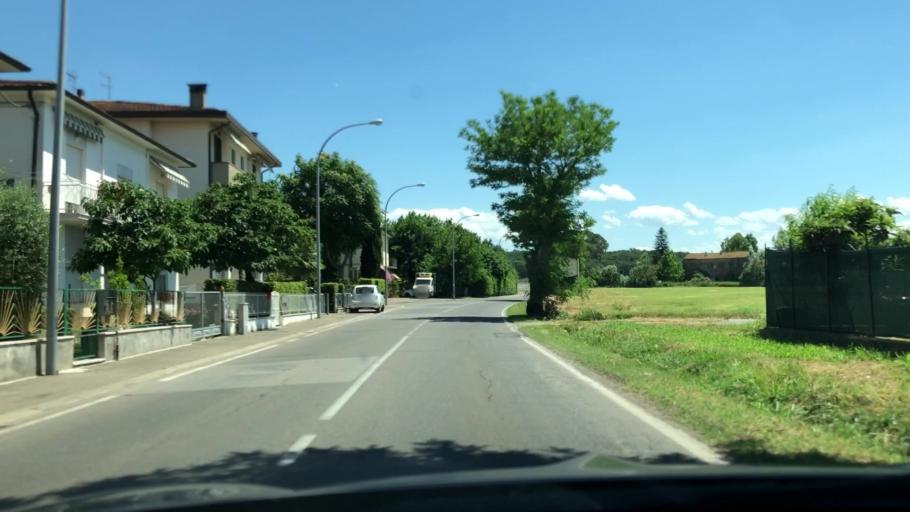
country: IT
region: Tuscany
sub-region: Province of Pisa
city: Ponsacco
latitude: 43.6146
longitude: 10.6413
